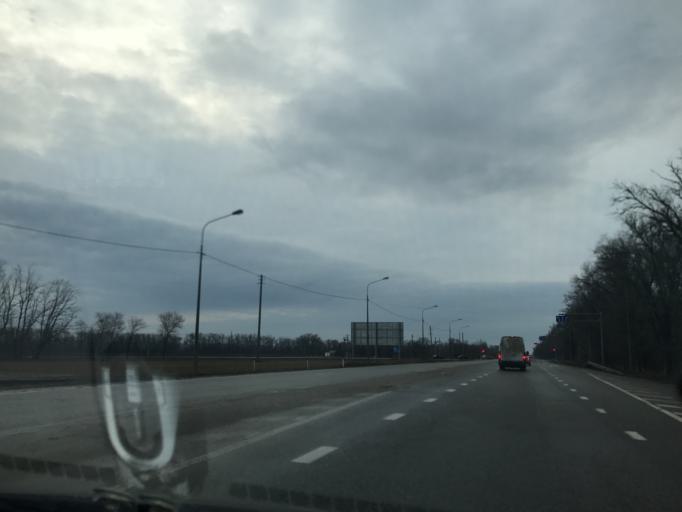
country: RU
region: Krasnodarskiy
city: Tikhoretsk
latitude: 45.8823
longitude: 40.1344
